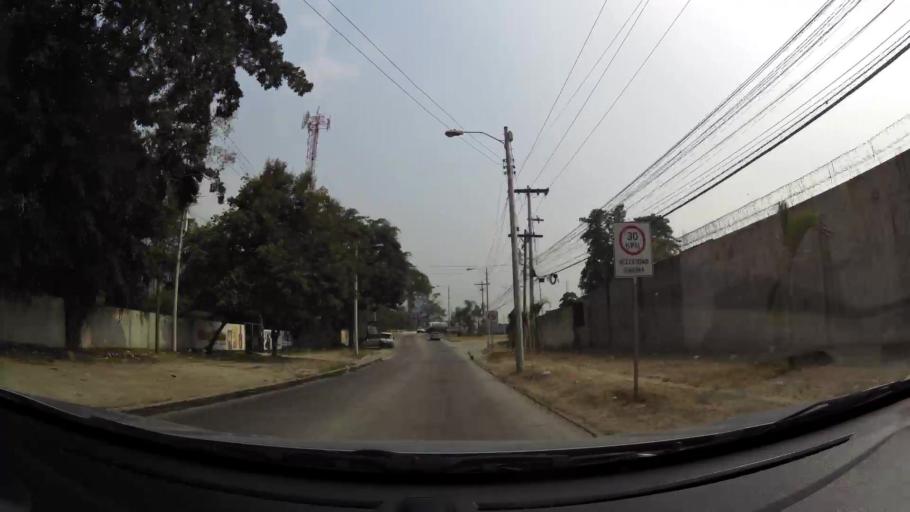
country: HN
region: Cortes
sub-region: San Pedro Sula
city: Pena Blanca
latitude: 15.5389
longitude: -88.0329
